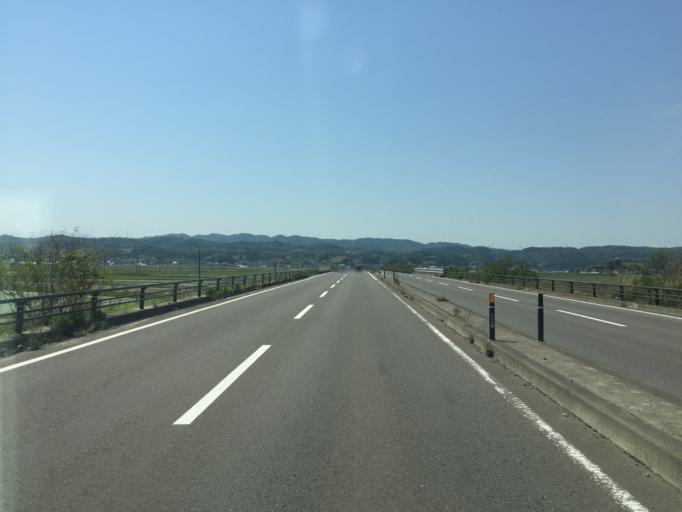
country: JP
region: Miyagi
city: Iwanuma
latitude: 38.1421
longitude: 140.8711
